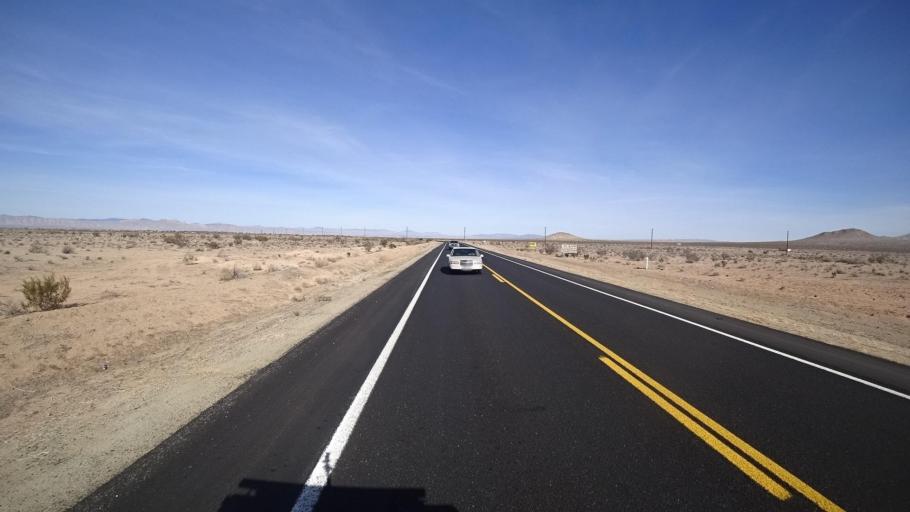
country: US
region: California
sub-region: Kern County
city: California City
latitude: 35.0989
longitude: -117.9174
